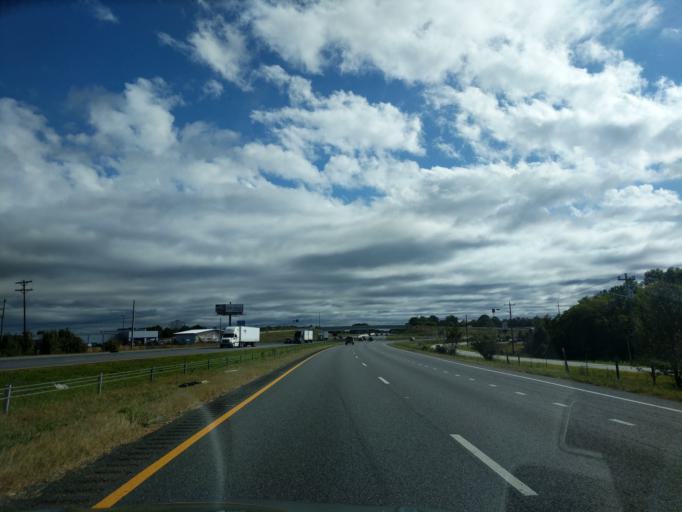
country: US
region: South Carolina
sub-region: Cherokee County
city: Gaffney
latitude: 35.0972
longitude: -81.6759
